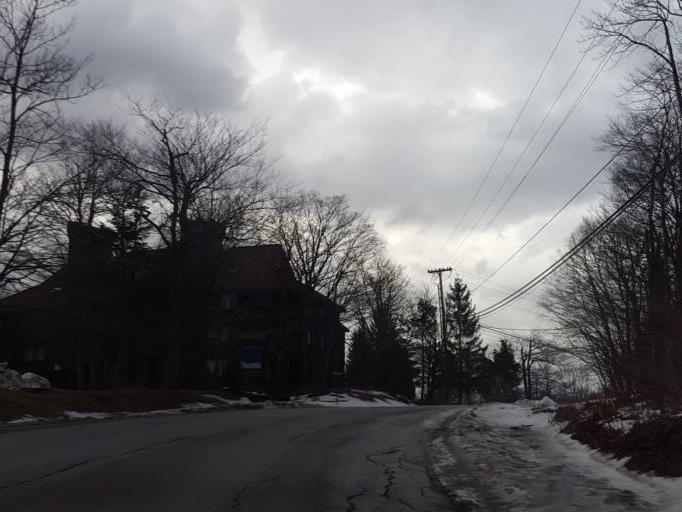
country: US
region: Vermont
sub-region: Rutland County
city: Rutland
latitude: 43.6310
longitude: -72.7798
